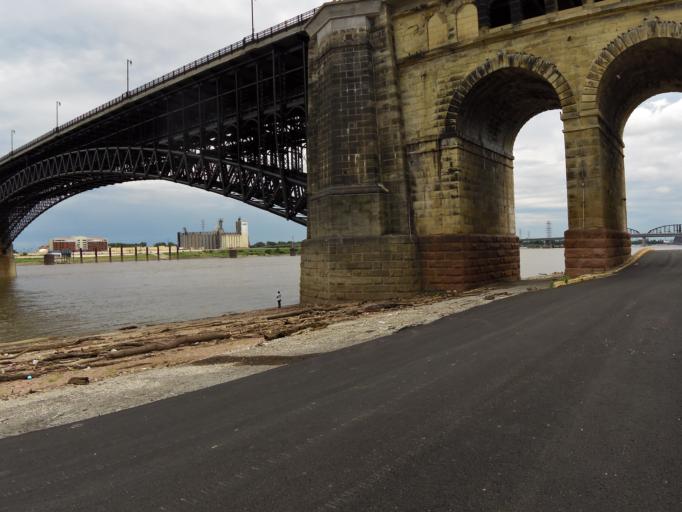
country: US
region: Missouri
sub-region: City of Saint Louis
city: St. Louis
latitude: 38.6296
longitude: -90.1821
